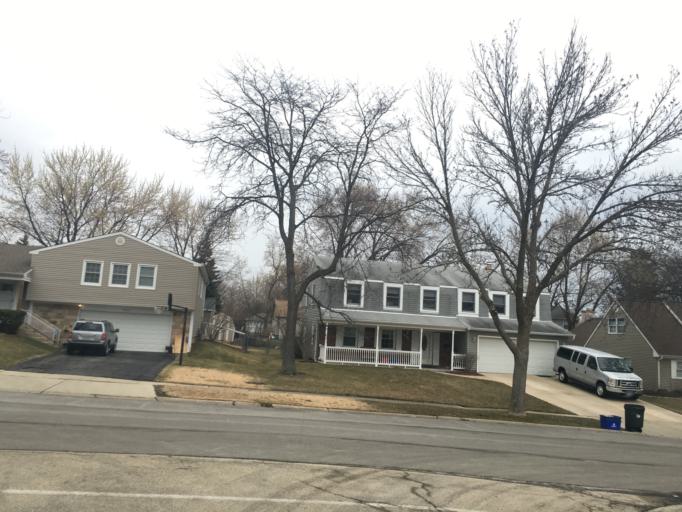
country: US
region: Illinois
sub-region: DuPage County
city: Hanover Park
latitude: 42.0308
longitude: -88.1240
